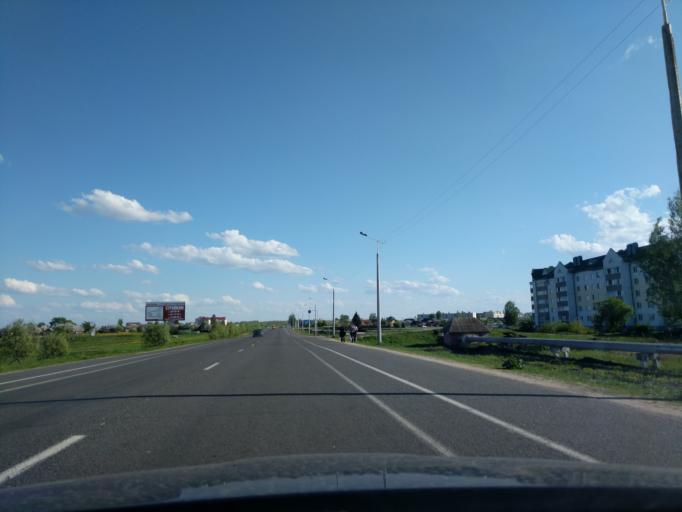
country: BY
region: Minsk
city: Myadzyel
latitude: 54.8819
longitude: 26.9391
